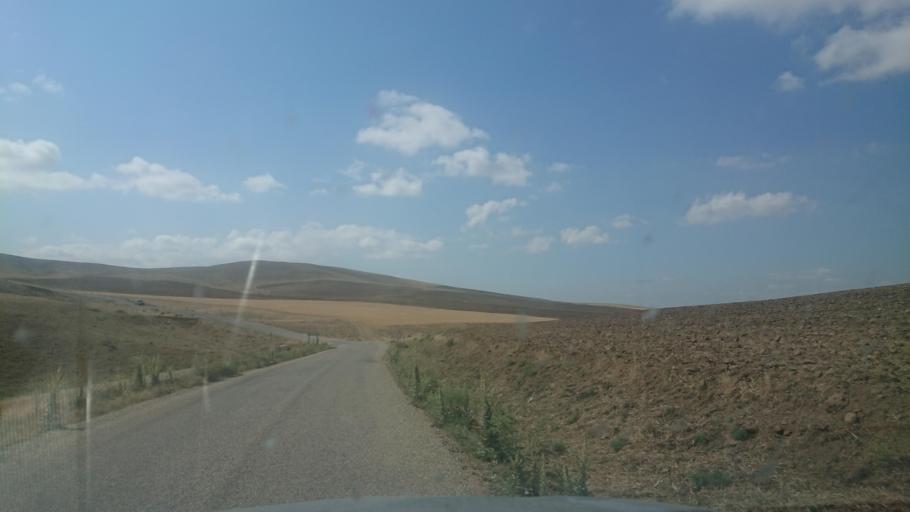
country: TR
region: Aksaray
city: Sariyahsi
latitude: 39.0088
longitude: 33.9496
